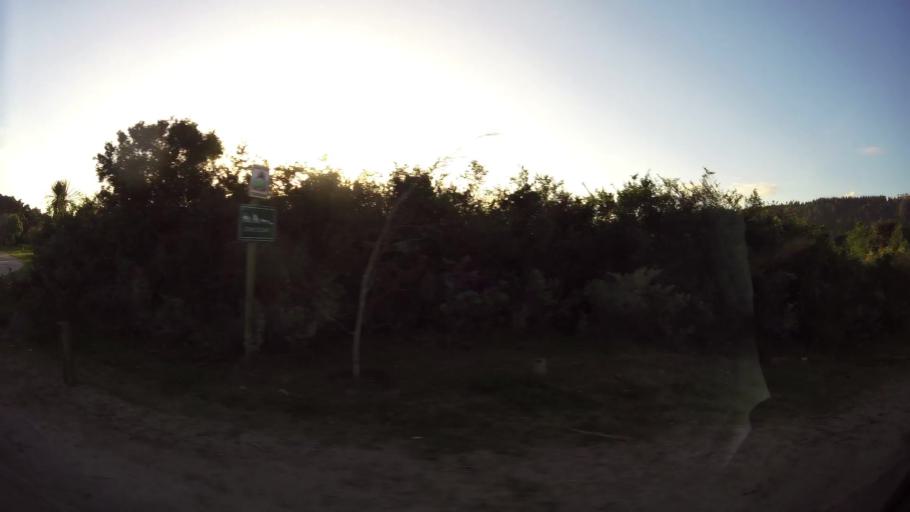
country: ZA
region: Western Cape
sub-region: Eden District Municipality
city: Knysna
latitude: -34.0146
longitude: 22.7875
